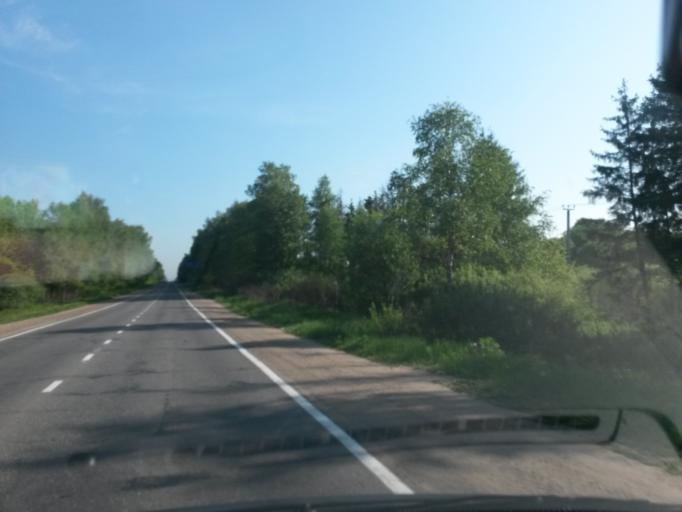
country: RU
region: Jaroslavl
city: Pereslavl'-Zalesskiy
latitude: 56.7728
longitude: 38.8767
